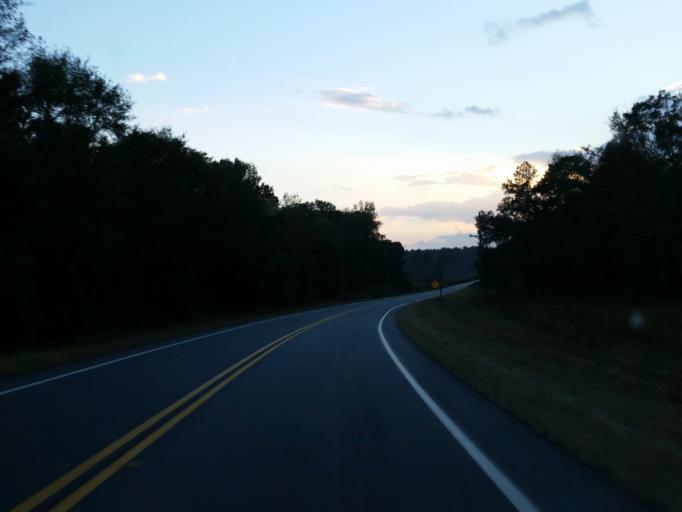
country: US
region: Georgia
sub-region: Pulaski County
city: Hawkinsville
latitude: 32.2419
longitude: -83.4996
